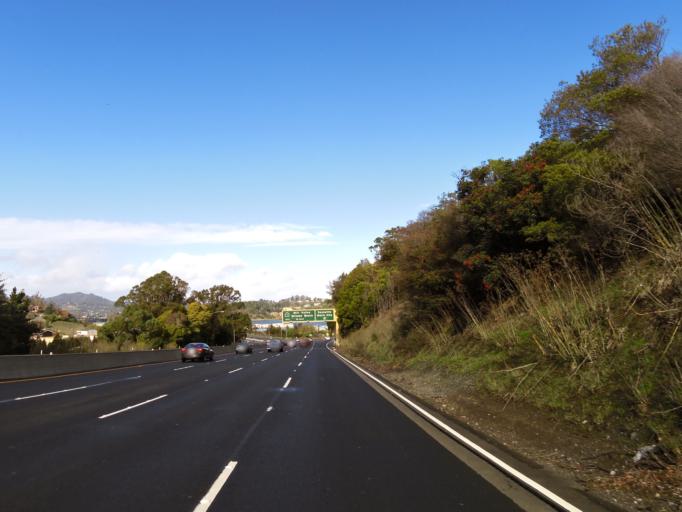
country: US
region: California
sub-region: Marin County
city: Marin City
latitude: 37.8690
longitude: -122.5070
